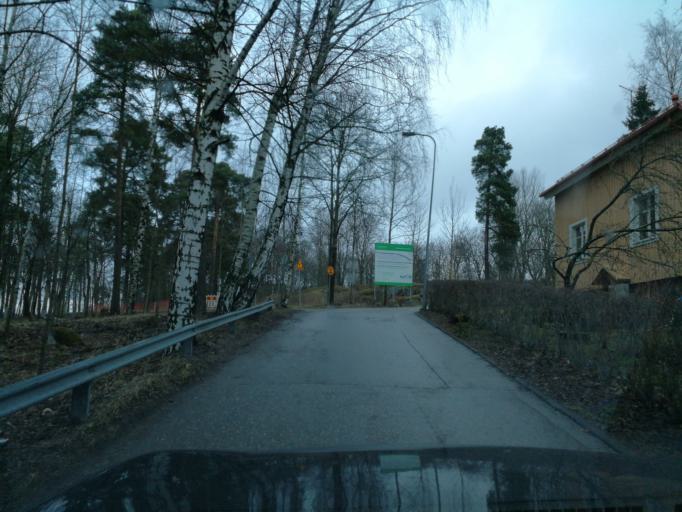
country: FI
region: Uusimaa
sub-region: Helsinki
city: Helsinki
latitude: 60.2114
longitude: 24.9372
